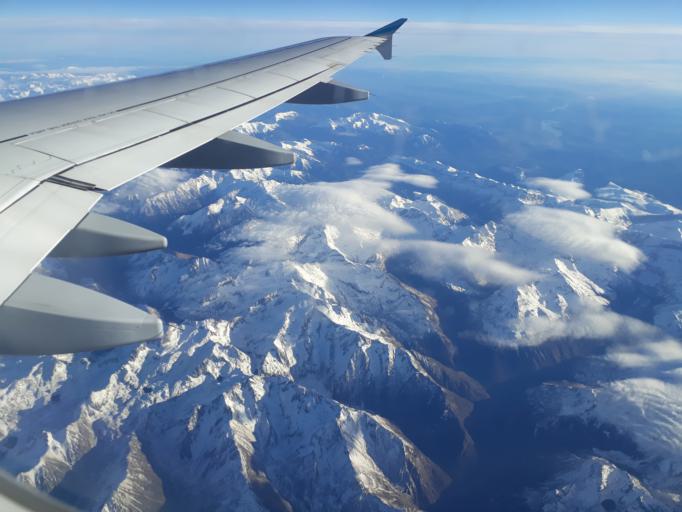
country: FR
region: Midi-Pyrenees
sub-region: Departement des Hautes-Pyrenees
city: Luz-Saint-Sauveur
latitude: 42.9066
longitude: -0.0294
